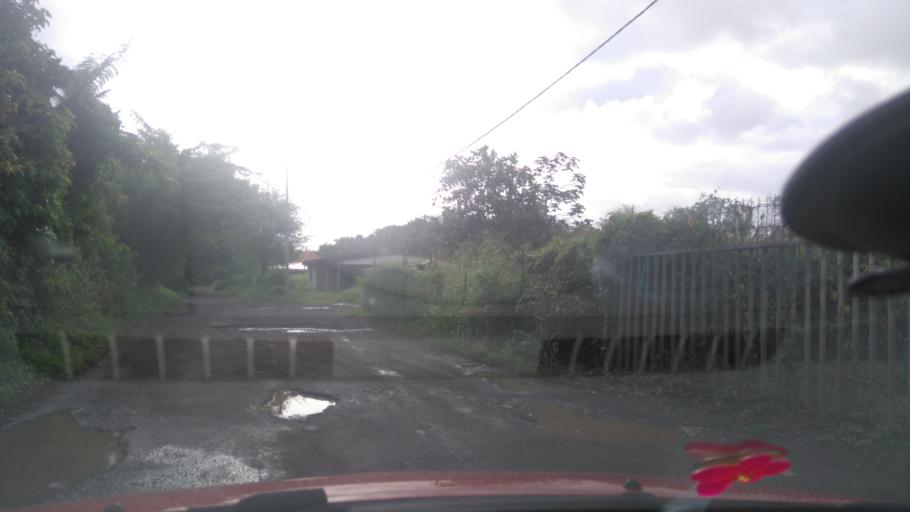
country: MQ
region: Martinique
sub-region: Martinique
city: Ducos
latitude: 14.5525
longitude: -60.9657
